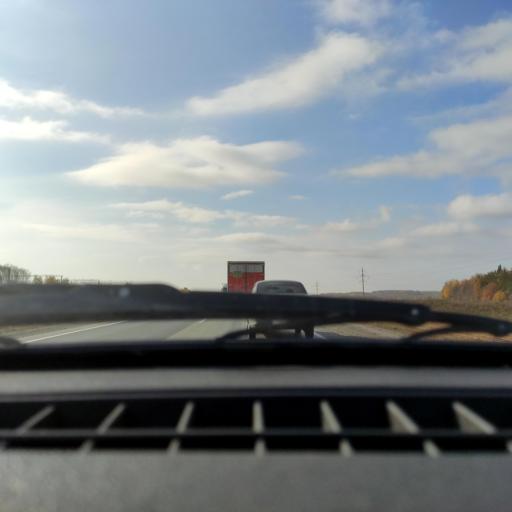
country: RU
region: Bashkortostan
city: Kabakovo
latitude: 54.7142
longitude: 56.2308
